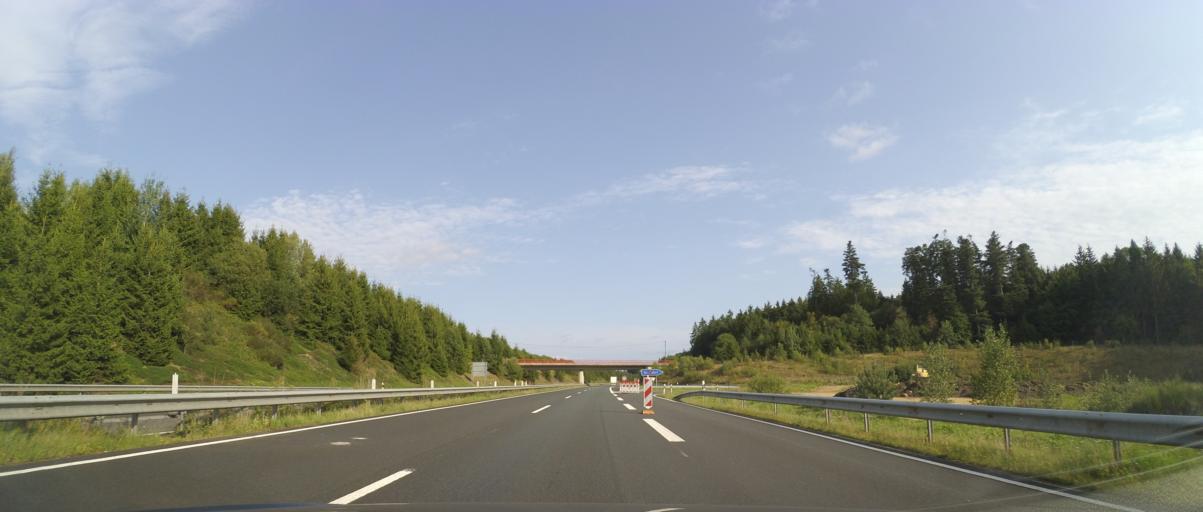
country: DE
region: Rheinland-Pfalz
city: Darscheid
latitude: 50.2075
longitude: 6.8807
